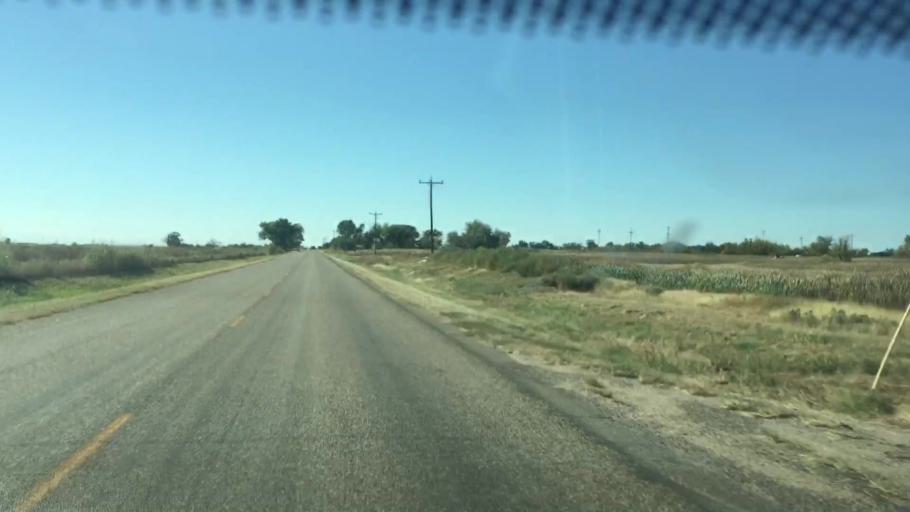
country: US
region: Colorado
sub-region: Prowers County
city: Lamar
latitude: 38.1152
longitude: -102.5850
